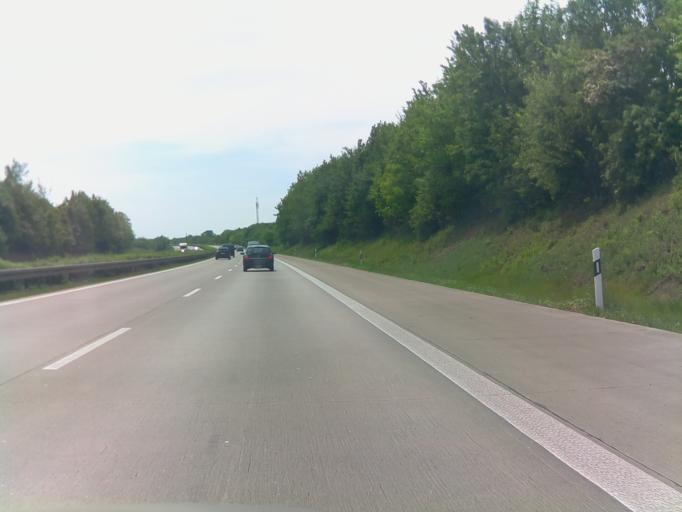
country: DE
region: Saxony-Anhalt
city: Hohendodeleben
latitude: 52.1153
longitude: 11.5280
